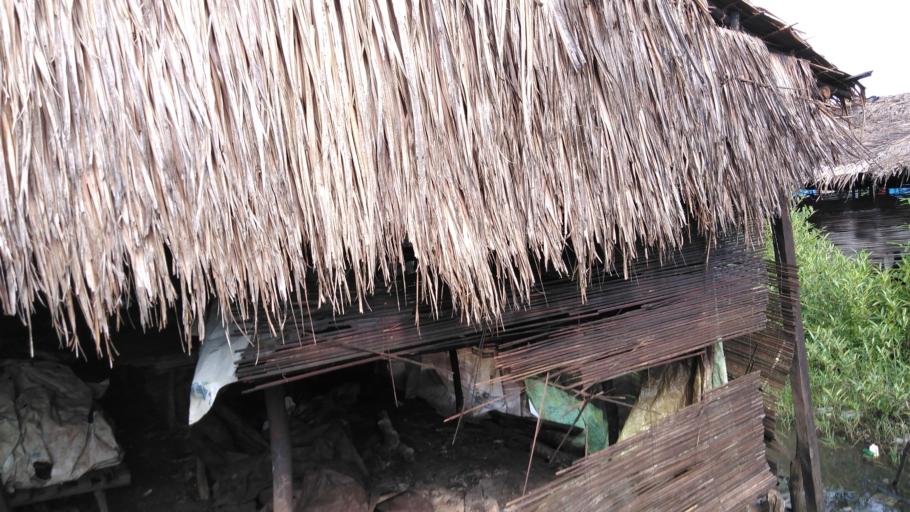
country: NG
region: Ondo
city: Igbekebo
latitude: 5.9301
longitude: 4.9596
